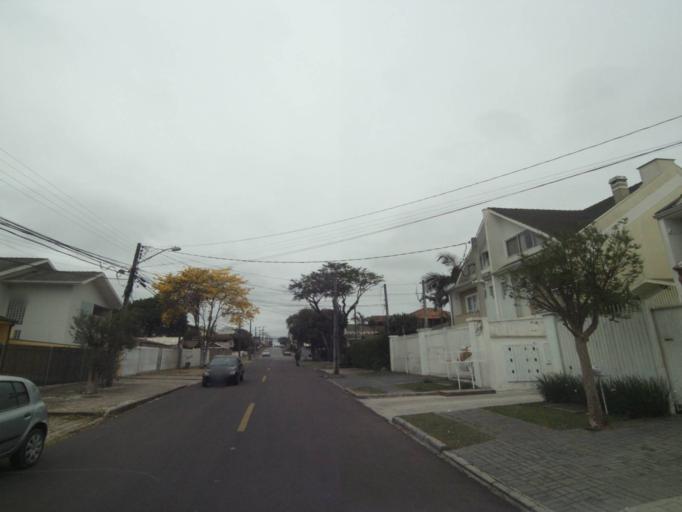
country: BR
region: Parana
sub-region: Pinhais
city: Pinhais
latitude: -25.4755
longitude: -49.2318
